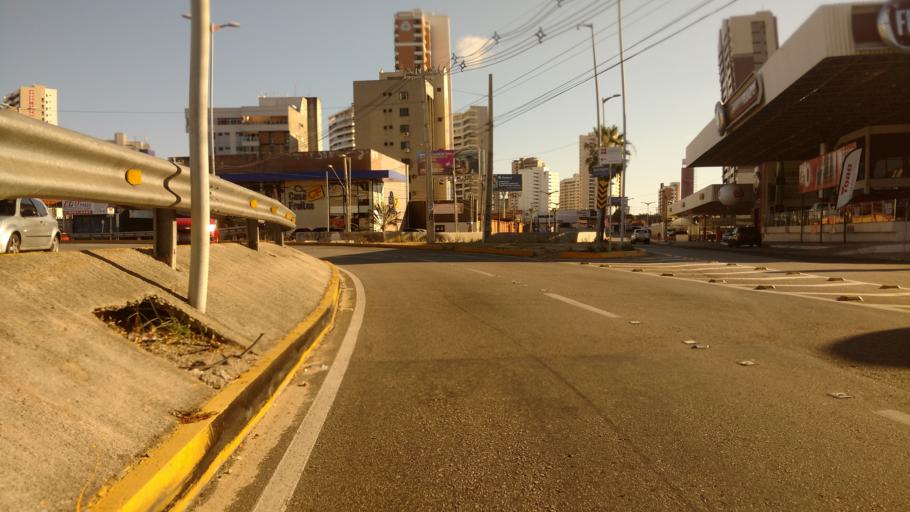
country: BR
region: Ceara
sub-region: Fortaleza
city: Fortaleza
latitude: -3.7564
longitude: -38.4915
